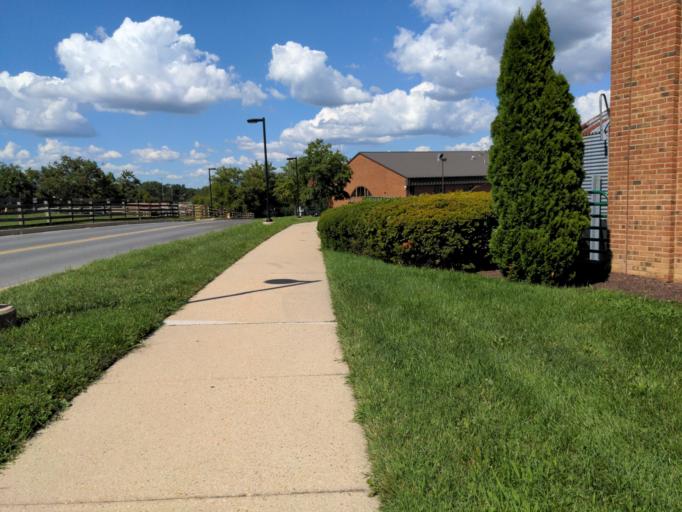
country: US
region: Maryland
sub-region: Prince George's County
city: College Park
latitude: 38.9920
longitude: -76.9402
